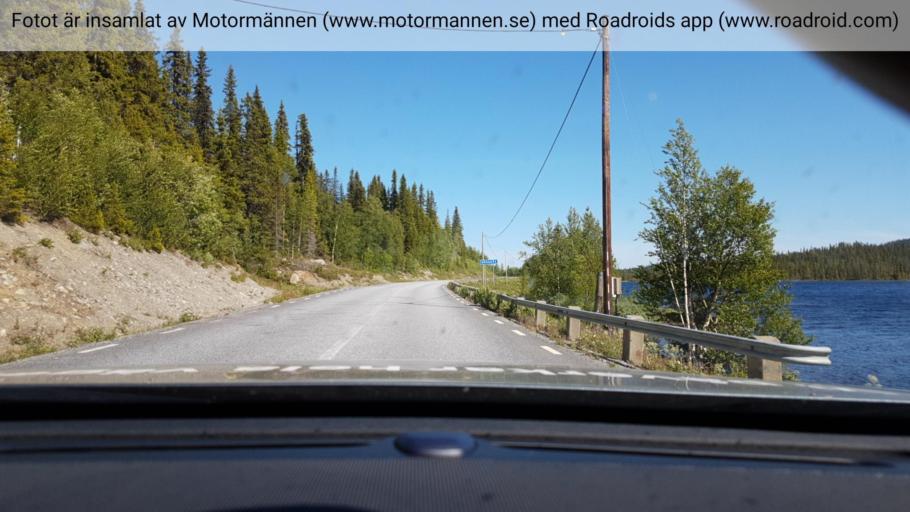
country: SE
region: Vaesterbotten
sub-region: Vilhelmina Kommun
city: Sjoberg
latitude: 64.9222
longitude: 15.6226
